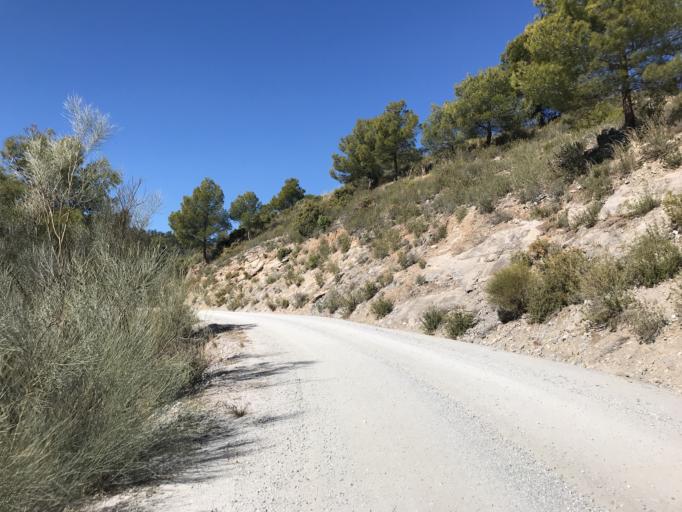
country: ES
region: Andalusia
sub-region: Provincia de Malaga
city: Canillas de Albaida
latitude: 36.8580
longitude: -3.9881
